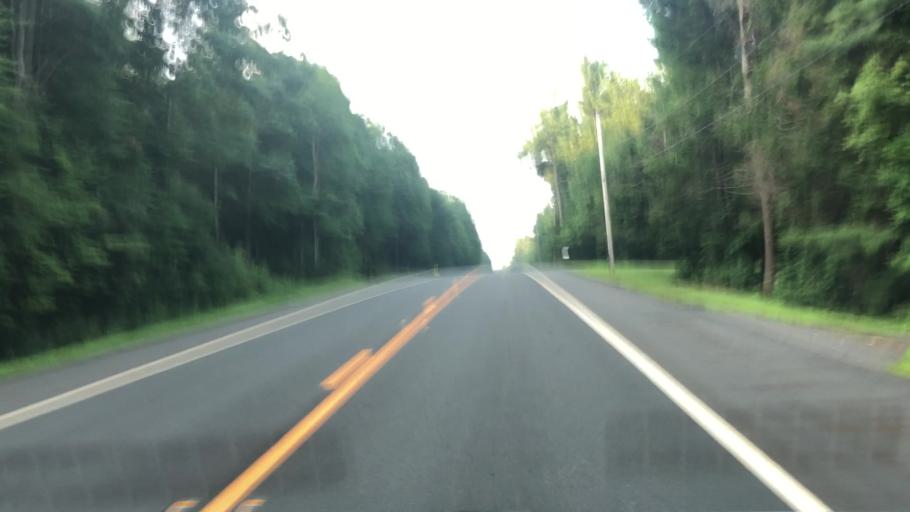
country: US
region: Massachusetts
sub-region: Franklin County
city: Ashfield
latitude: 42.4890
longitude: -72.8093
